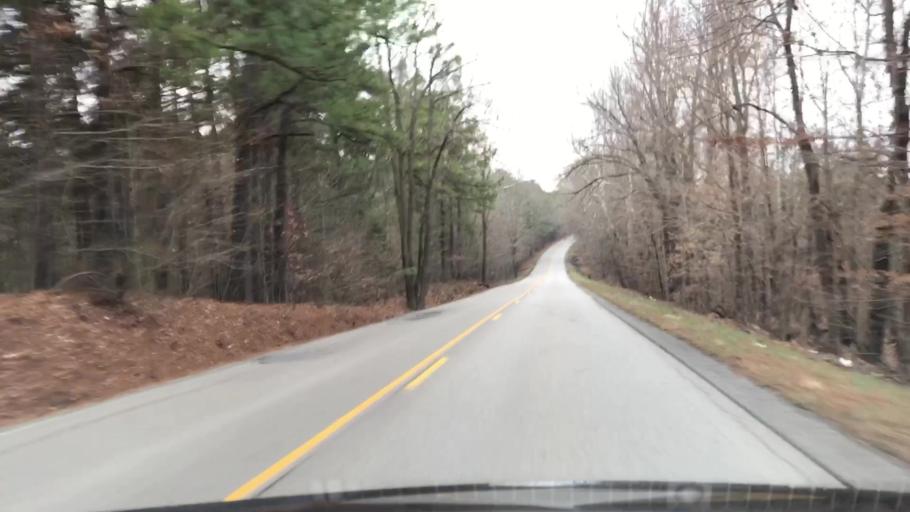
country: US
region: Kentucky
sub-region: Muhlenberg County
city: Morehead
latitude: 37.2843
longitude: -87.2099
